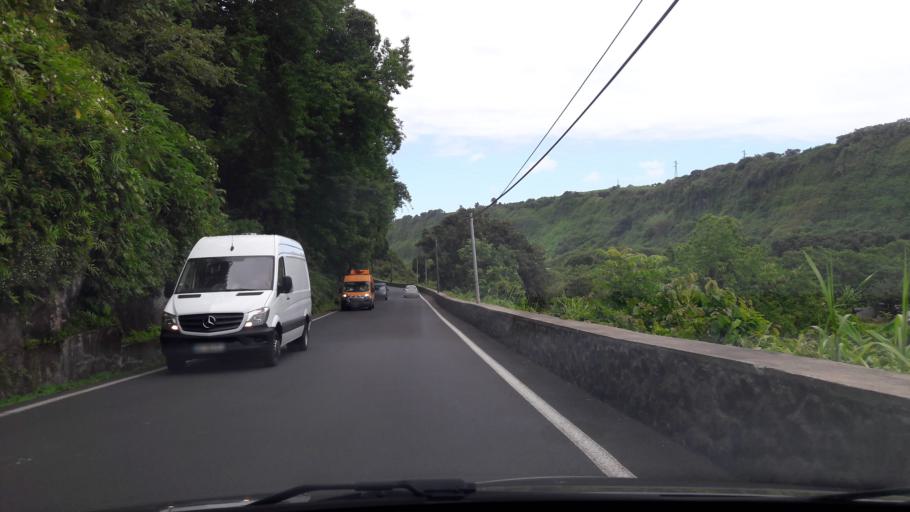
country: RE
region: Reunion
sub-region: Reunion
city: Saint-Andre
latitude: -20.9868
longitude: 55.6215
